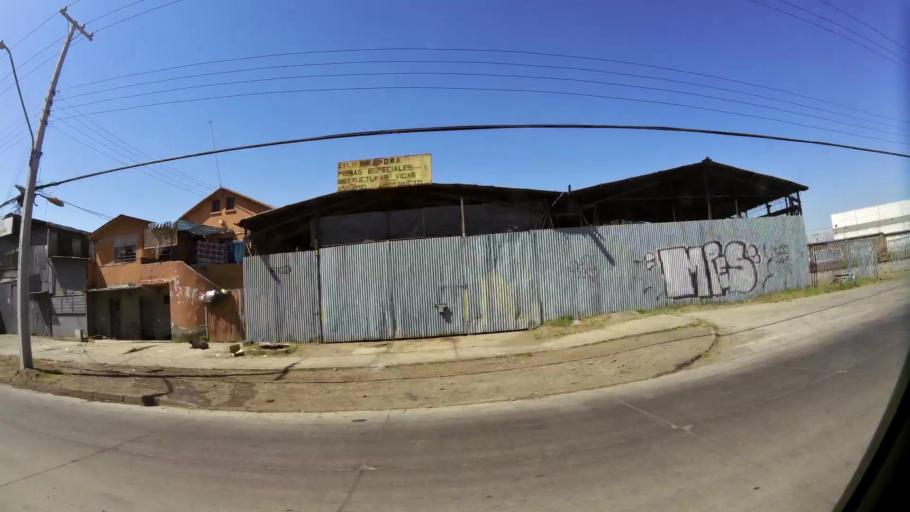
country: CL
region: Santiago Metropolitan
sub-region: Provincia de Santiago
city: Lo Prado
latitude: -33.5226
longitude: -70.7513
